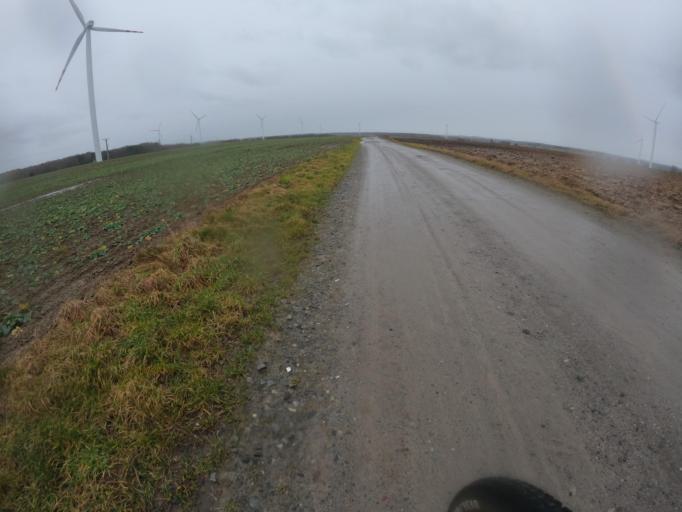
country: PL
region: West Pomeranian Voivodeship
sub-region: Powiat slawienski
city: Darlowo
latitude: 54.4008
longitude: 16.5287
